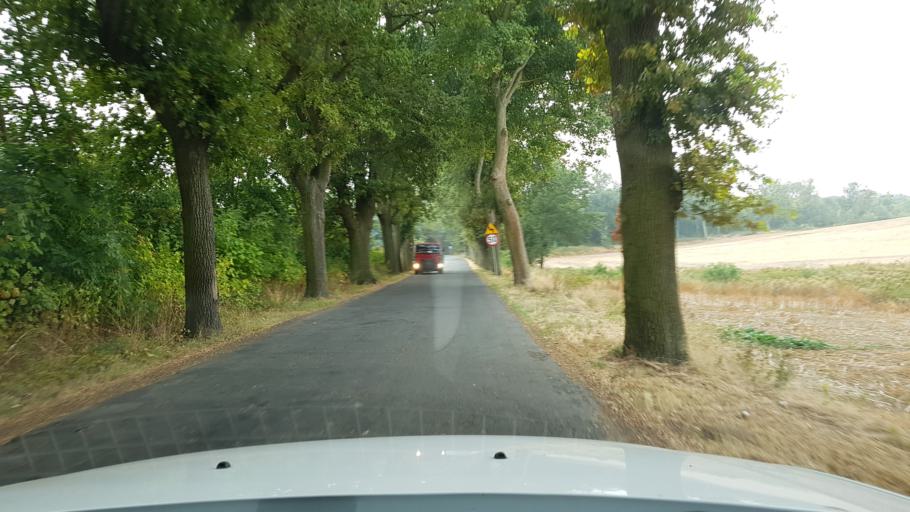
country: PL
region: West Pomeranian Voivodeship
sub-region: Powiat gryfinski
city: Moryn
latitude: 52.8764
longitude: 14.3786
